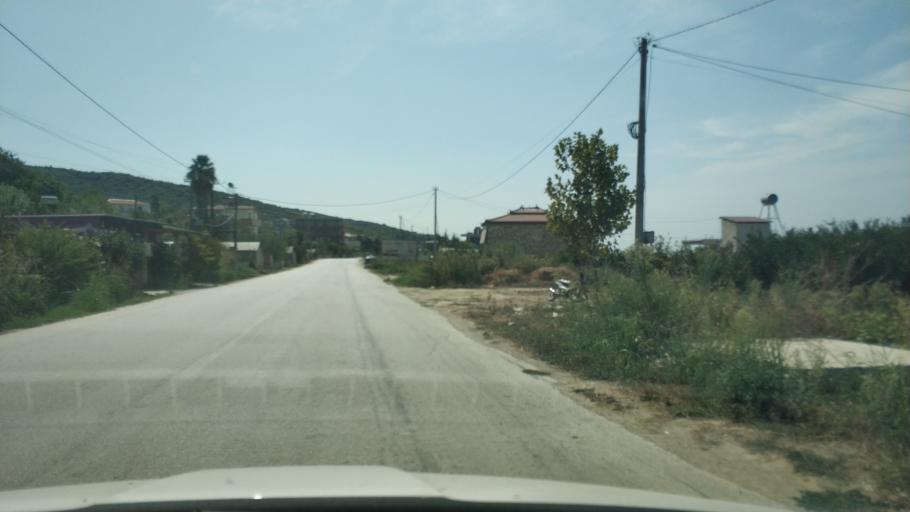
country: AL
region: Fier
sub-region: Rrethi i Lushnjes
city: Grabjan
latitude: 40.9424
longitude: 19.5376
